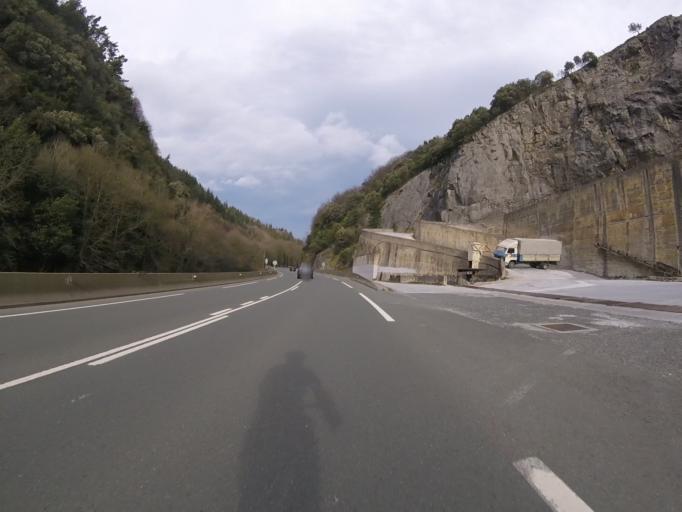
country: ES
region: Basque Country
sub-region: Provincia de Guipuzcoa
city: Cestona
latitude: 43.2470
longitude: -2.2599
